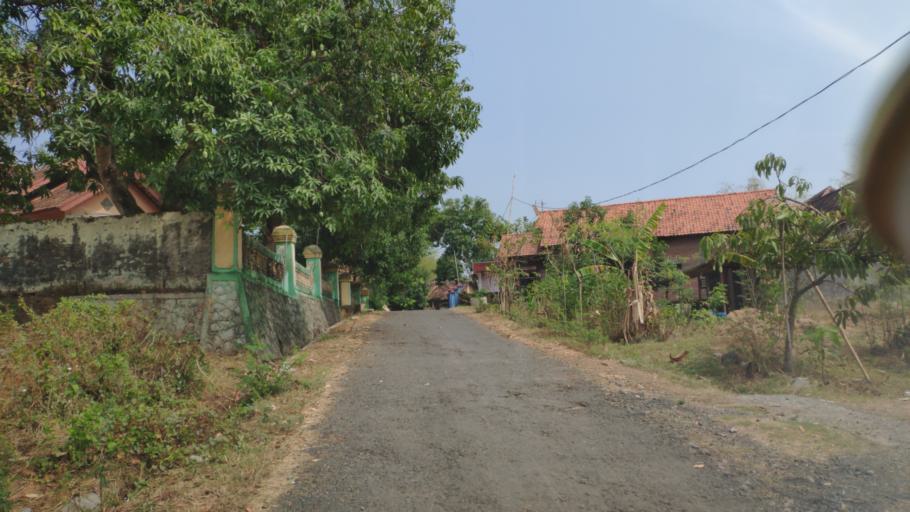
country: ID
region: Central Java
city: Sendangsari
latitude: -6.9778
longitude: 111.3386
